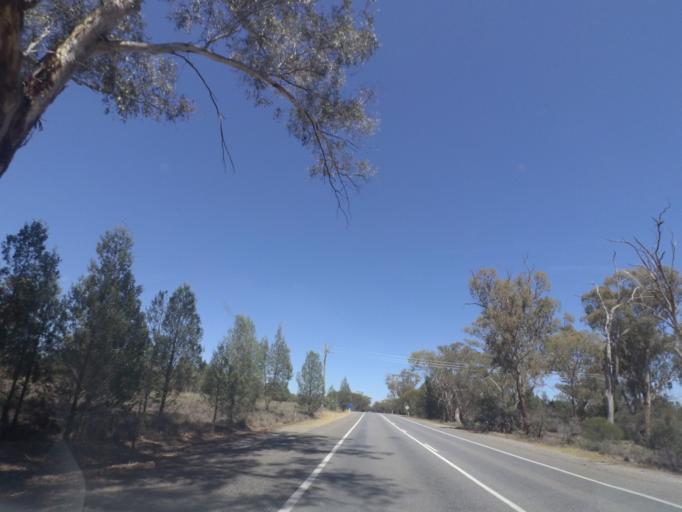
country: AU
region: New South Wales
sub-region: Narrandera
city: Narrandera
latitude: -34.7379
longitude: 146.5822
